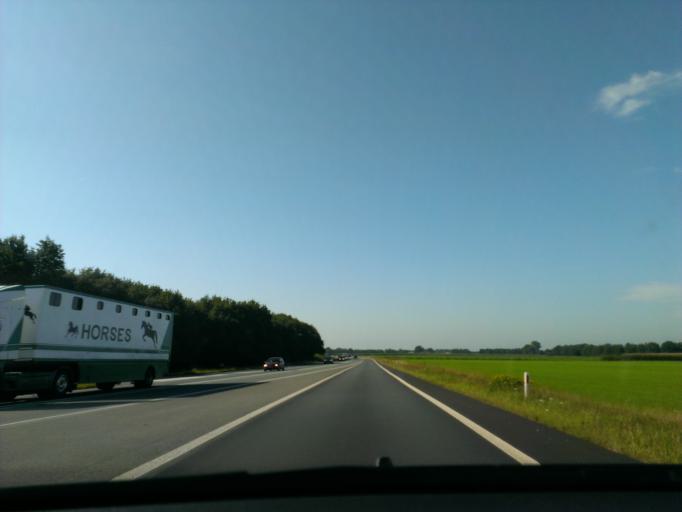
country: NL
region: Drenthe
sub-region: Gemeente Coevorden
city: Dalen
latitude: 52.7065
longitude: 6.7498
